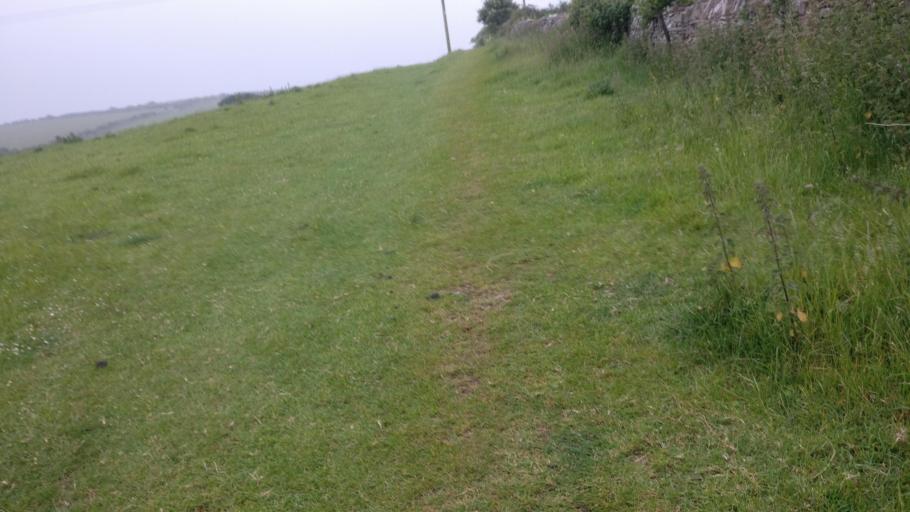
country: GB
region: England
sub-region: Dorset
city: Swanage
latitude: 50.6060
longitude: -2.0121
